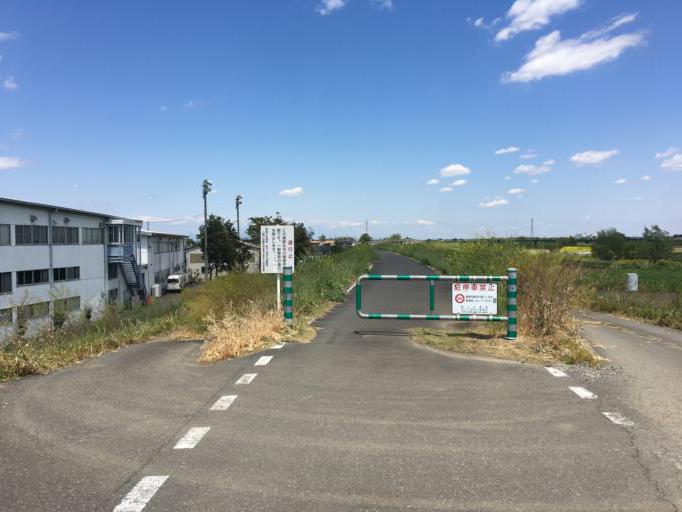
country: JP
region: Saitama
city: Kawagoe
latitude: 35.9358
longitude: 139.4625
